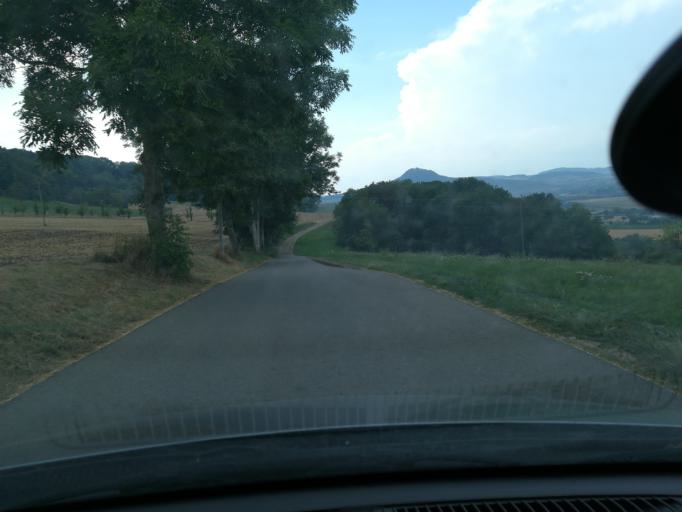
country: DE
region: Baden-Wuerttemberg
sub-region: Freiburg Region
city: Muhlhausen-Ehingen
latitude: 47.8067
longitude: 8.8045
